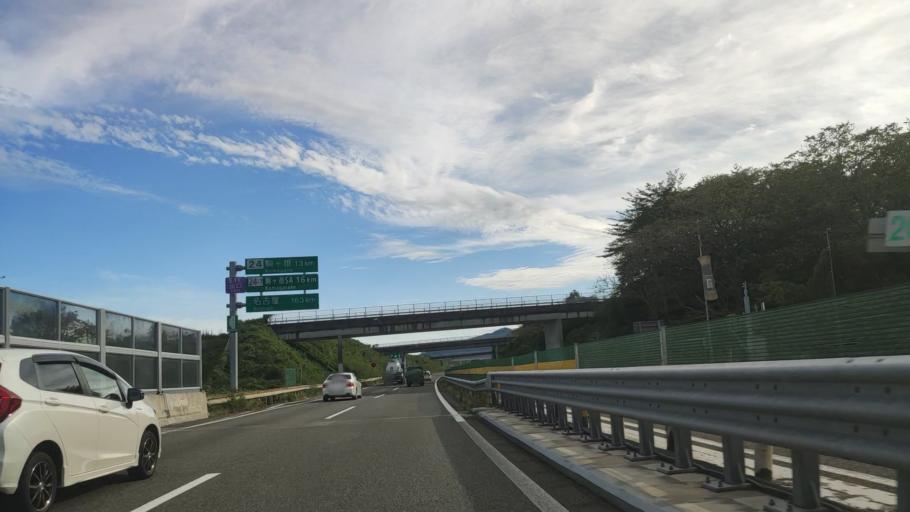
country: JP
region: Nagano
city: Ina
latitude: 35.8489
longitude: 137.9363
